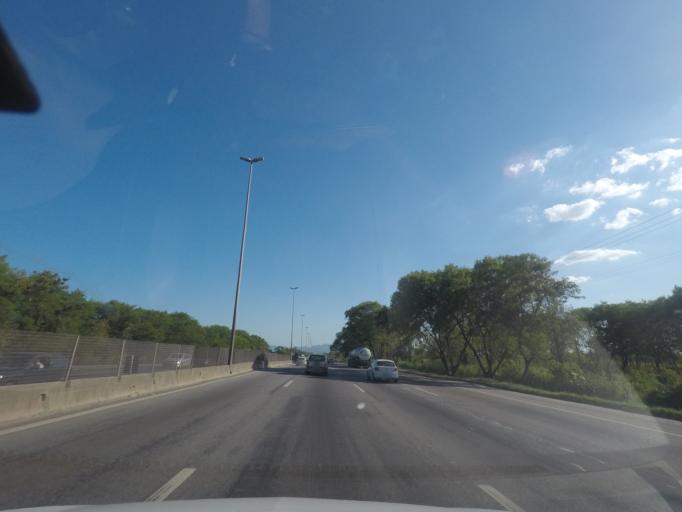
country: BR
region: Rio de Janeiro
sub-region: Duque De Caxias
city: Duque de Caxias
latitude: -22.7257
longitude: -43.2892
